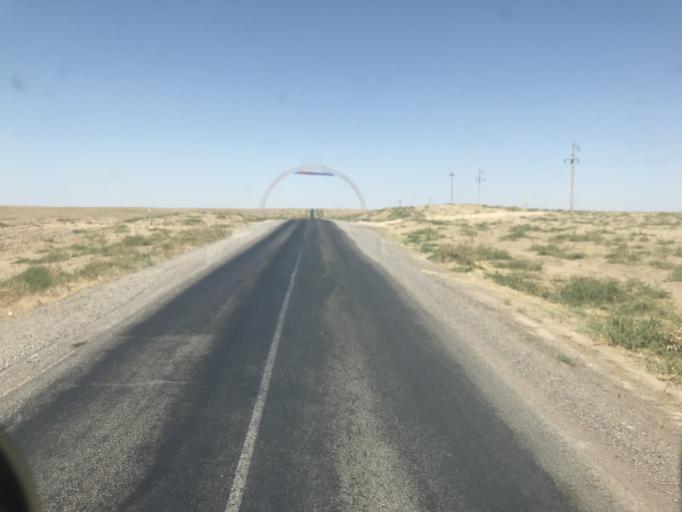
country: UZ
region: Toshkent
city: Chinoz
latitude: 41.1370
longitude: 68.7115
